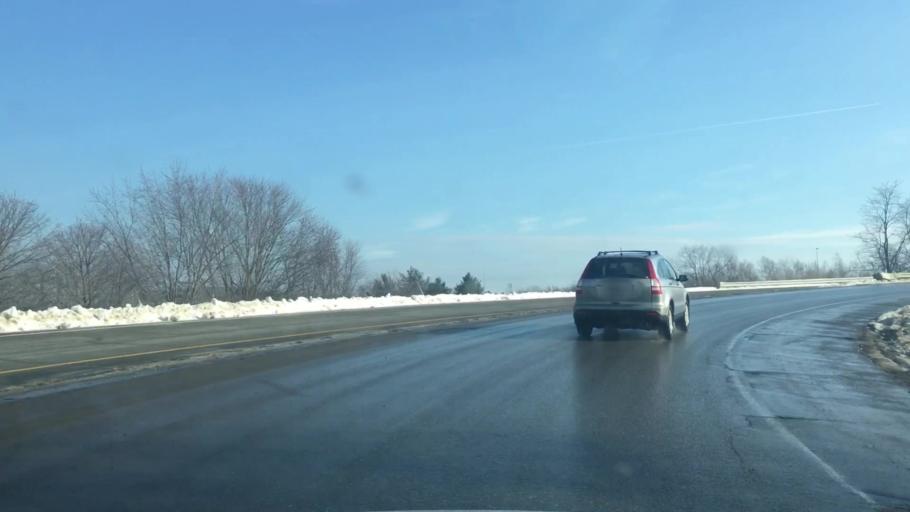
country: US
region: Maine
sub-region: Penobscot County
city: Brewer
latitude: 44.7853
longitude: -68.7702
